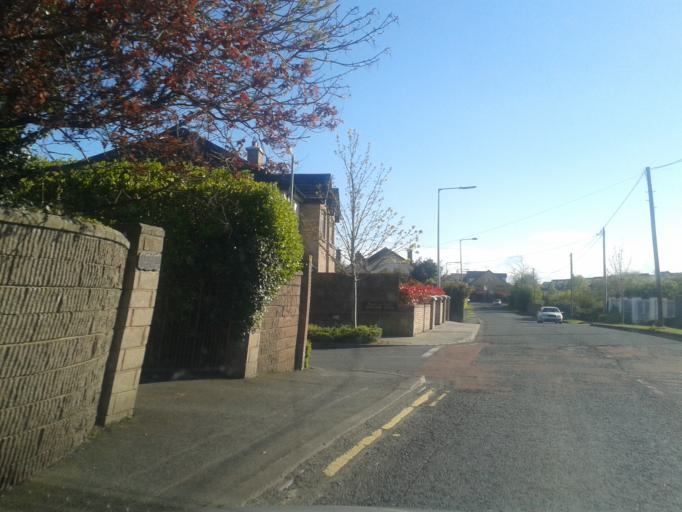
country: IE
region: Leinster
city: Kinsealy-Drinan
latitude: 53.4518
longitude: -6.1845
